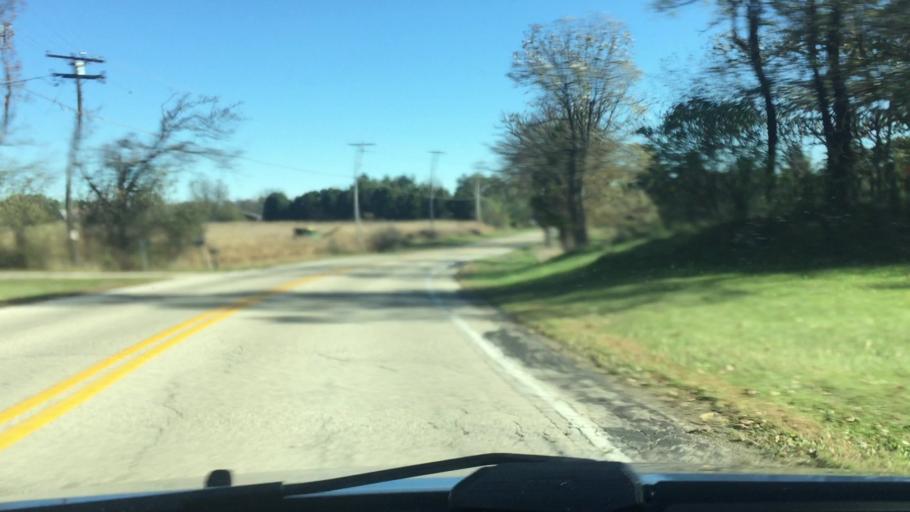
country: US
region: Wisconsin
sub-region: Waukesha County
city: North Prairie
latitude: 42.9444
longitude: -88.4205
